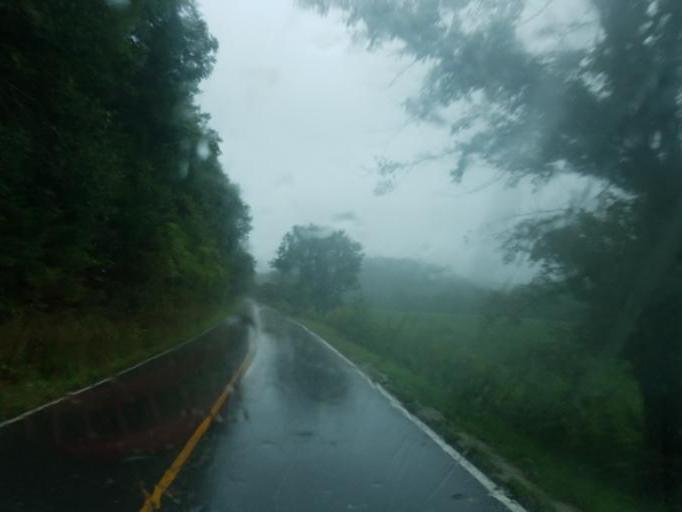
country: US
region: Kentucky
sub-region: Carter County
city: Grayson
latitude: 38.4711
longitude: -83.0403
